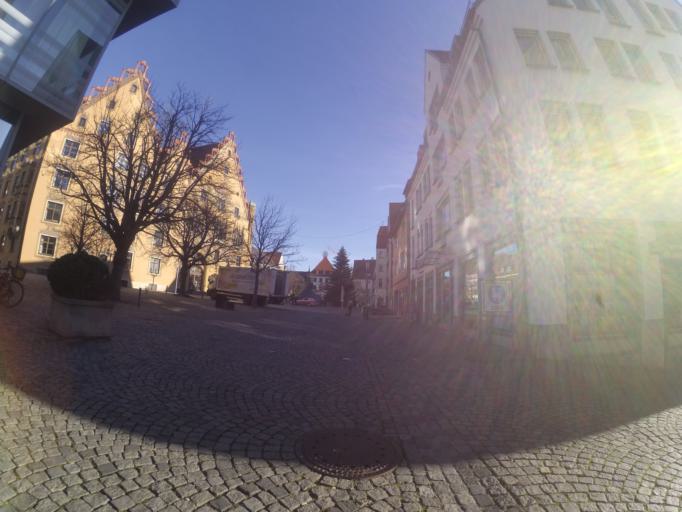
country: DE
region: Baden-Wuerttemberg
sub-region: Tuebingen Region
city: Ulm
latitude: 48.3965
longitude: 9.9928
